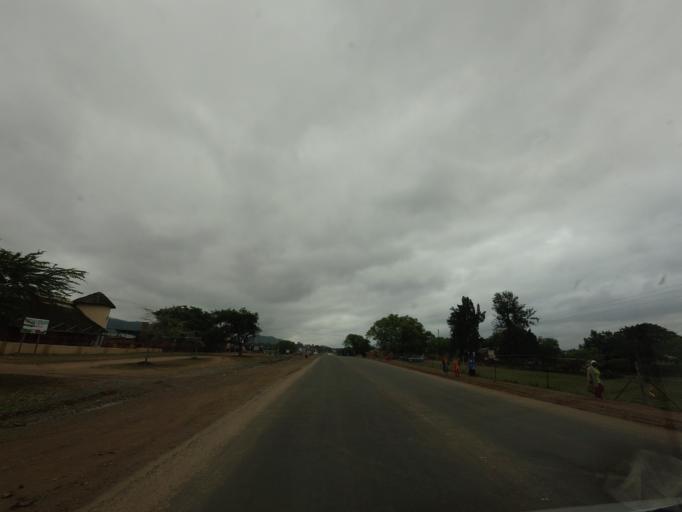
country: SZ
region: Hhohho
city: Ntfonjeni
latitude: -25.6962
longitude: 31.4977
